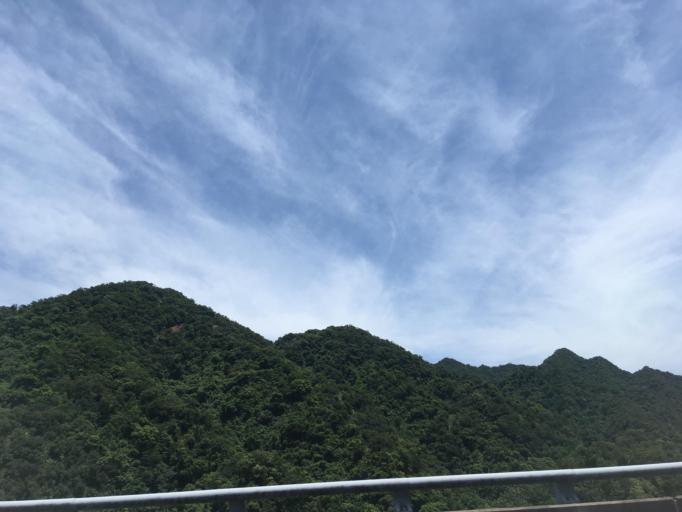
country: TW
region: Taipei
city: Taipei
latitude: 24.9813
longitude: 121.6726
